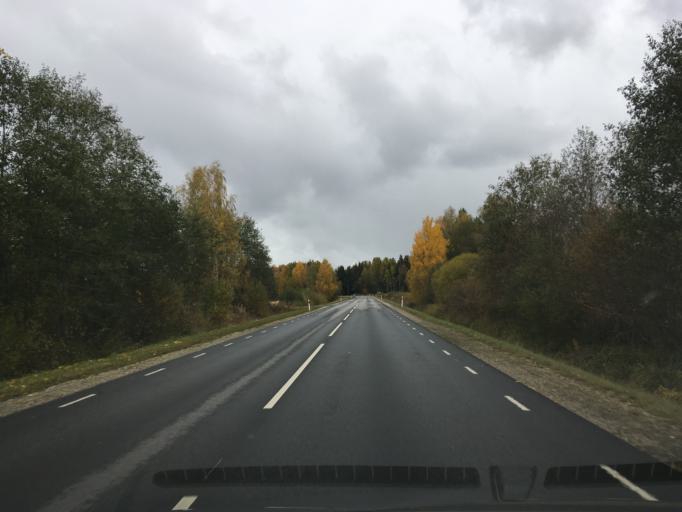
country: EE
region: Harju
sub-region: Anija vald
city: Kehra
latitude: 59.3151
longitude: 25.3436
